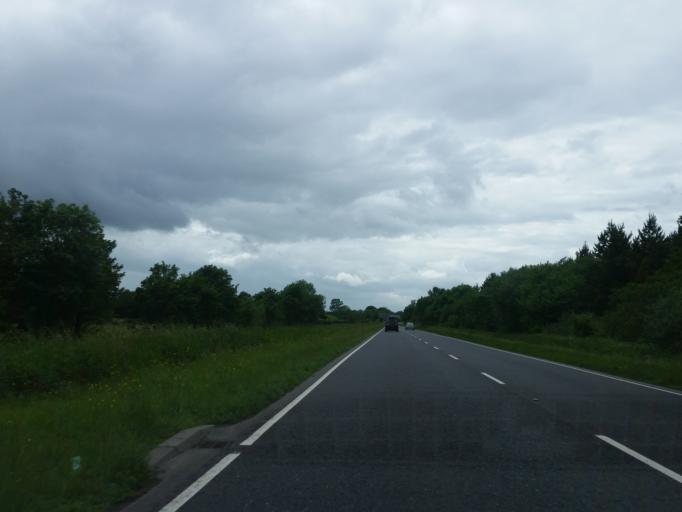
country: GB
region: Northern Ireland
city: Fivemiletown
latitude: 54.3844
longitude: -7.2586
